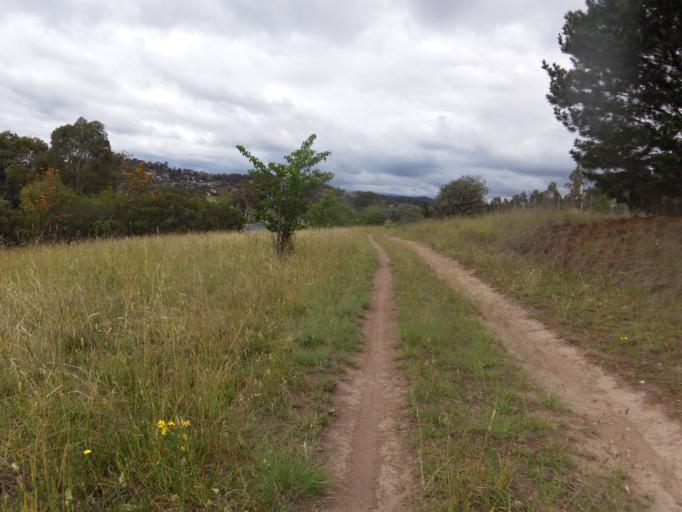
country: AU
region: Australian Capital Territory
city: Macquarie
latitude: -35.3404
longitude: 149.0274
